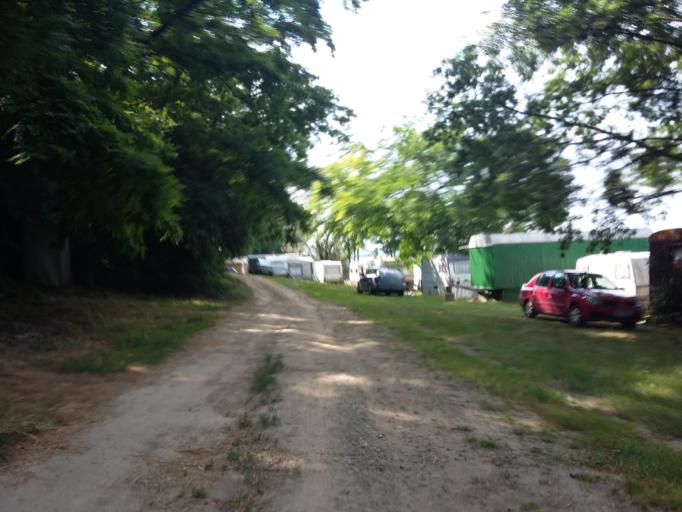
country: CZ
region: South Moravian
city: Sakvice
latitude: 48.8857
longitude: 16.6628
